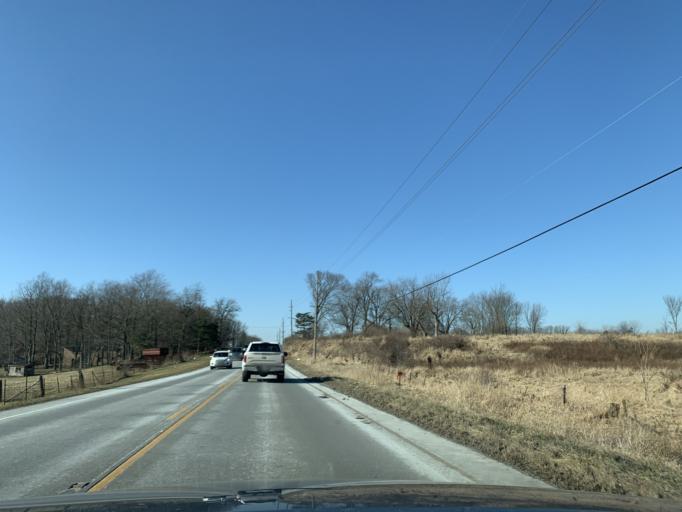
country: US
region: Indiana
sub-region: Lake County
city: Crown Point
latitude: 41.4207
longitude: -87.4049
